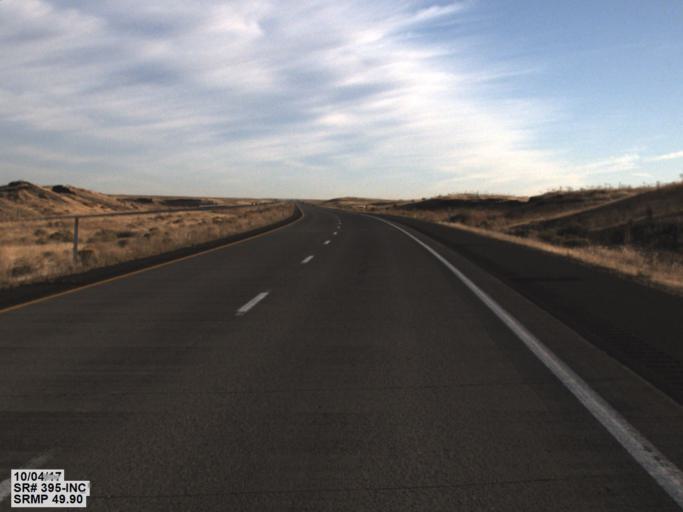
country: US
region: Washington
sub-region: Franklin County
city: Connell
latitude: 46.6018
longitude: -118.9275
